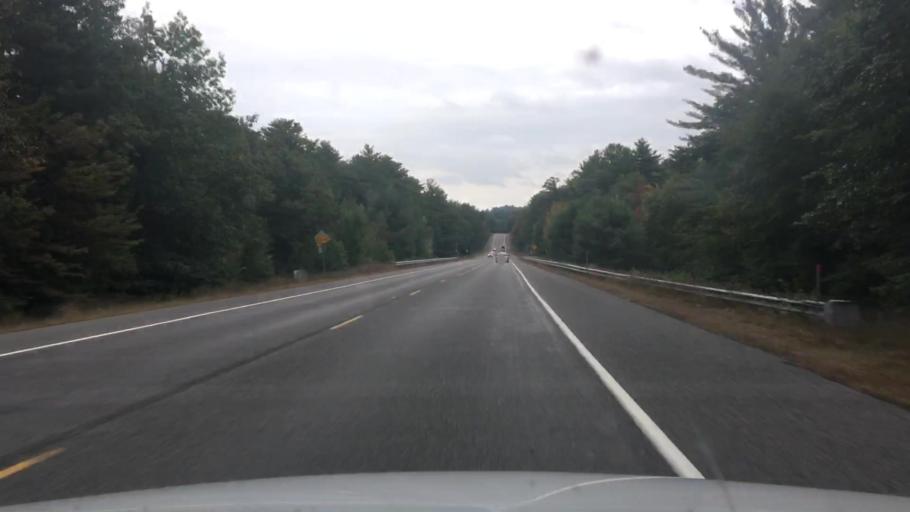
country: US
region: New Hampshire
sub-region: Carroll County
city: Wolfeboro
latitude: 43.5001
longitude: -71.2617
